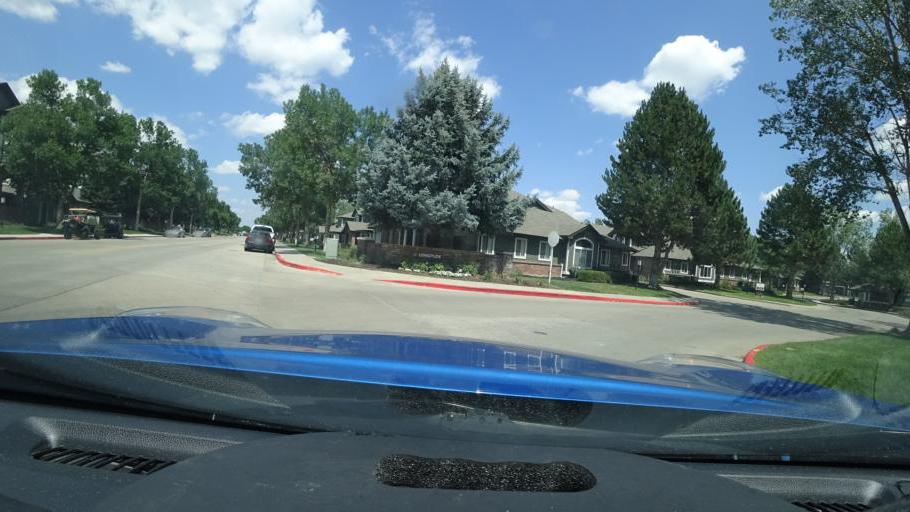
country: US
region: Colorado
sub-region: Arapahoe County
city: Glendale
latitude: 39.6991
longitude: -104.8886
